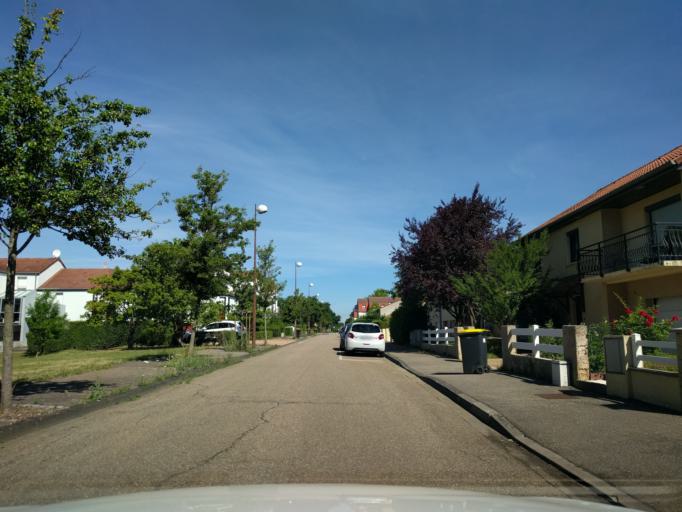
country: FR
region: Lorraine
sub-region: Departement de la Moselle
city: Peltre
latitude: 49.0973
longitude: 6.2434
